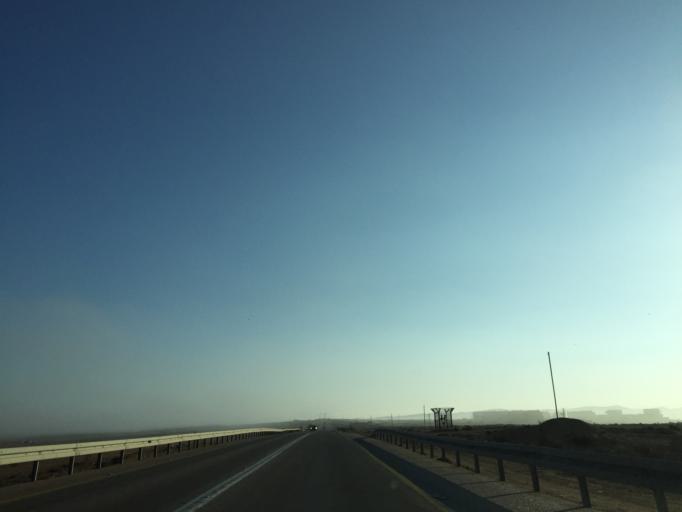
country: IL
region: Southern District
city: Yeroham
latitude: 30.9968
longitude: 34.9289
